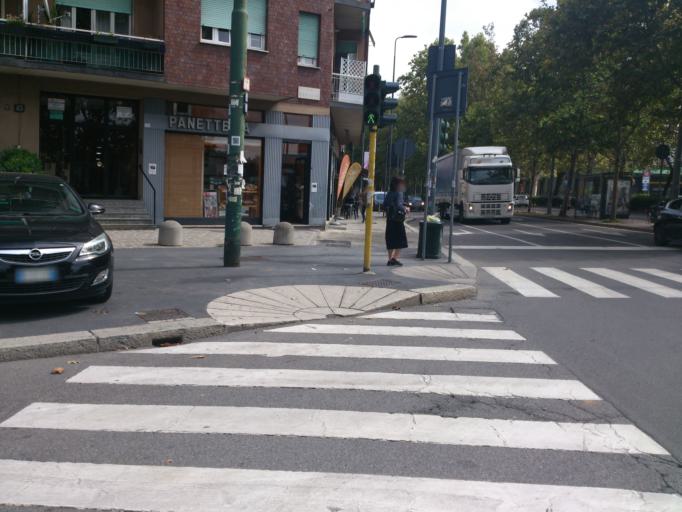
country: IT
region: Lombardy
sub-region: Citta metropolitana di Milano
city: Milano
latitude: 45.4450
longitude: 9.1633
